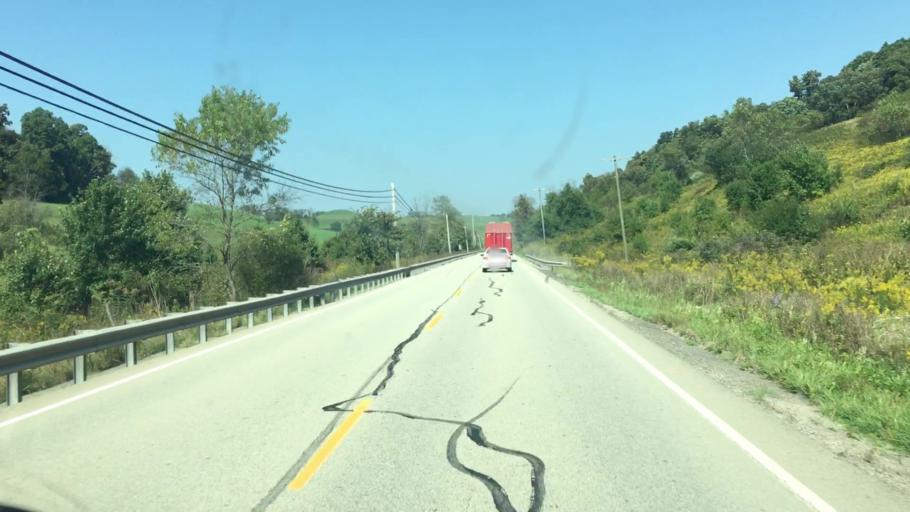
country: US
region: Pennsylvania
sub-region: Washington County
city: Washington
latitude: 40.0544
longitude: -80.2971
